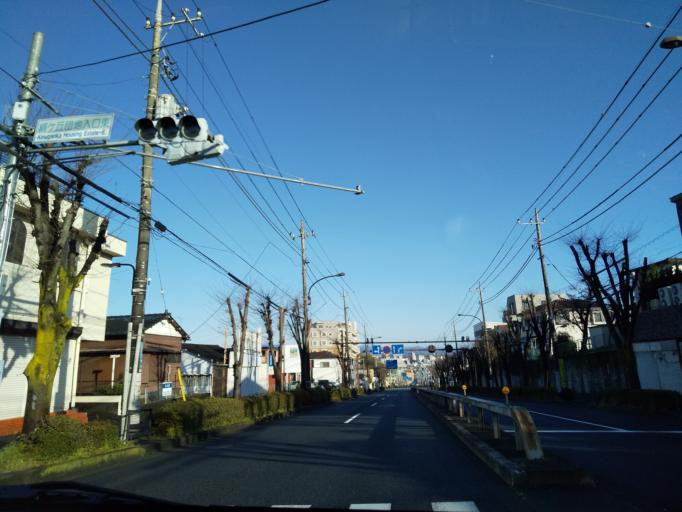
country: JP
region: Tokyo
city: Hachioji
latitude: 35.6374
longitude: 139.3611
